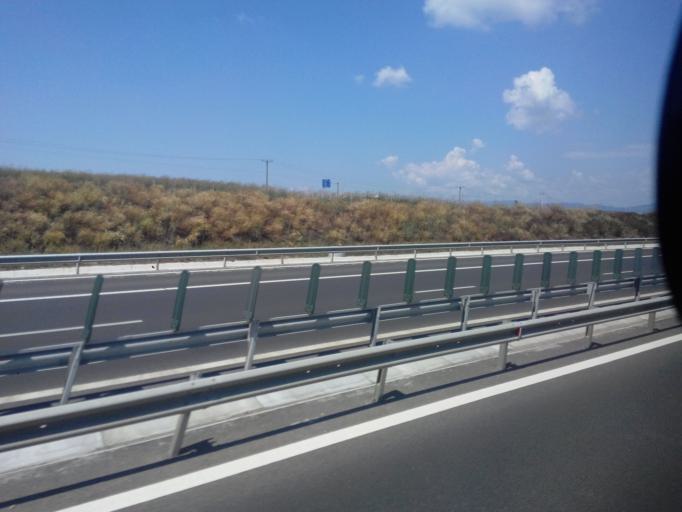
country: RO
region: Alba
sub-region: Municipiul Sebes
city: Sebes
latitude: 45.9429
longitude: 23.5940
